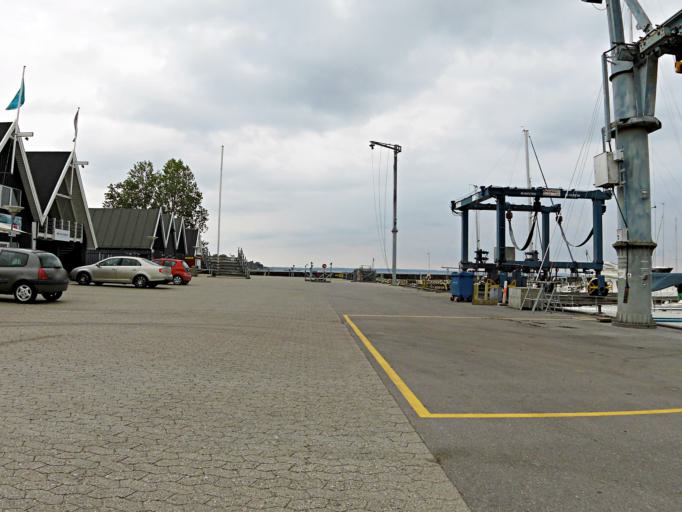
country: DK
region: Capital Region
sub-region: Horsholm Kommune
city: Horsholm
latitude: 55.8863
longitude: 12.5443
